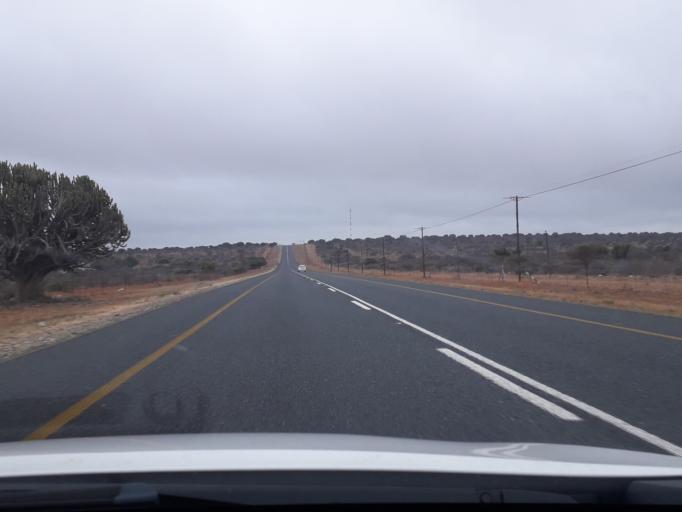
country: ZA
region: Limpopo
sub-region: Vhembe District Municipality
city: Louis Trichardt
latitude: -23.4141
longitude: 29.7541
